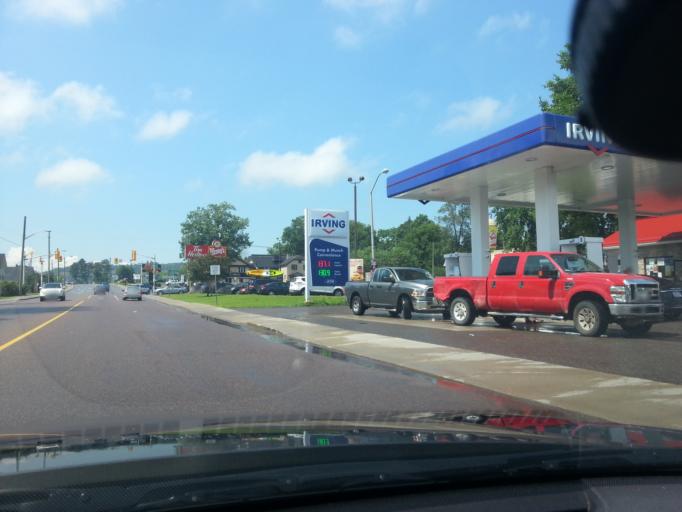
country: CA
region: Ontario
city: Renfrew
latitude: 45.4783
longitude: -76.6965
